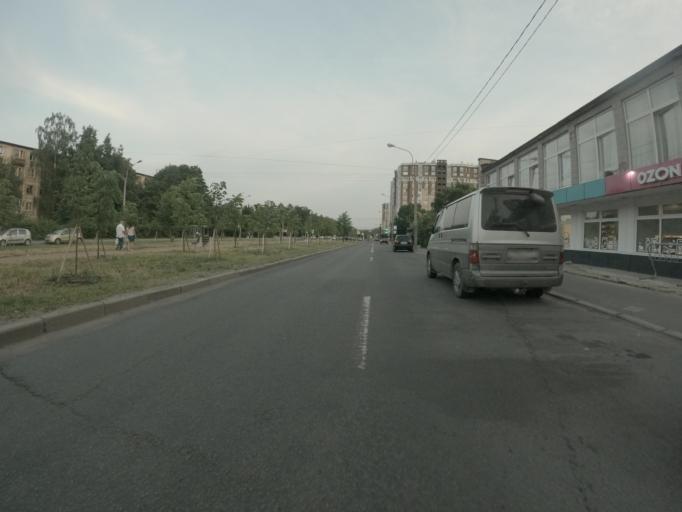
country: RU
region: Leningrad
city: Kalininskiy
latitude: 59.9726
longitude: 30.3982
